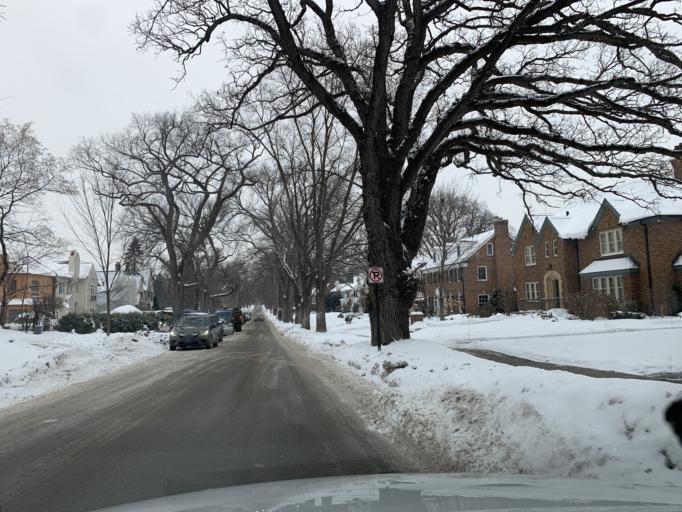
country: US
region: Minnesota
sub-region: Hennepin County
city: Edina
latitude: 44.9149
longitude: -93.3434
